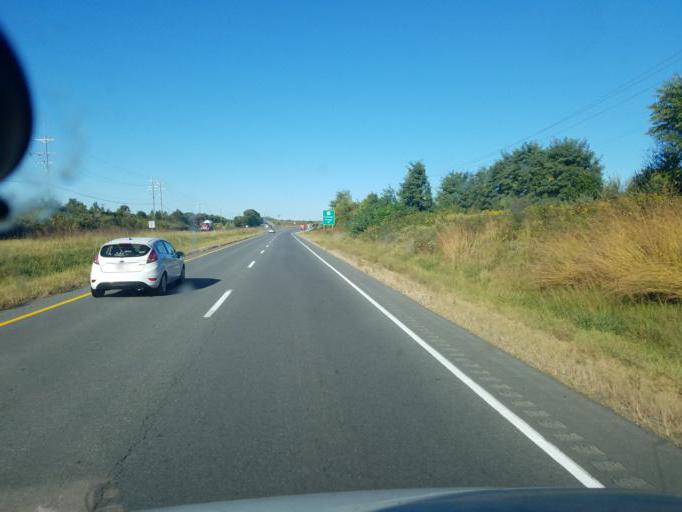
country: US
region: Virginia
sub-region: Culpeper County
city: Culpeper
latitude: 38.4452
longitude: -78.0013
